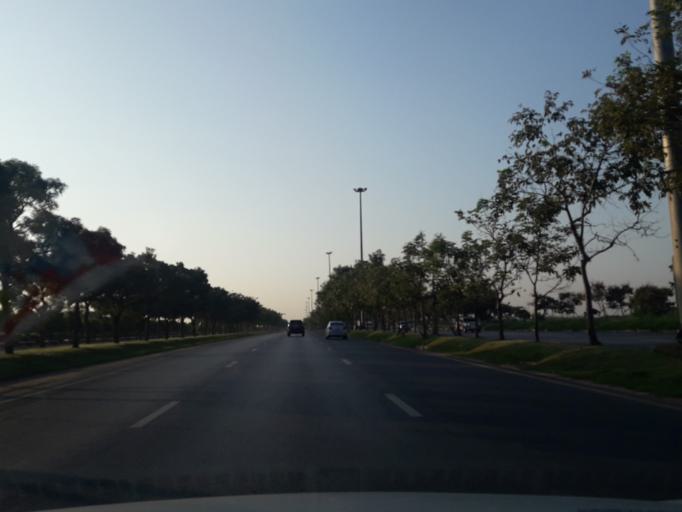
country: TH
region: Phra Nakhon Si Ayutthaya
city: Bang Pa-in
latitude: 14.2158
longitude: 100.5439
